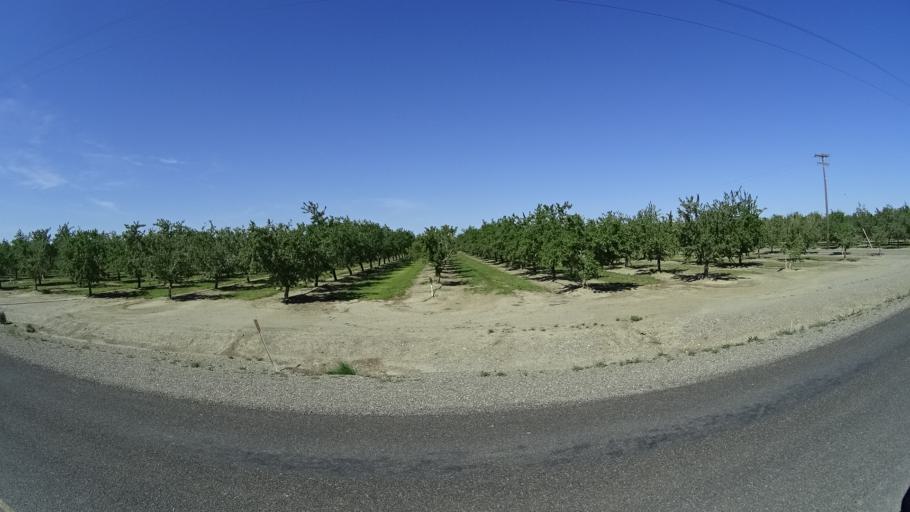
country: US
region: California
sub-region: Glenn County
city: Hamilton City
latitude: 39.6892
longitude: -122.1032
